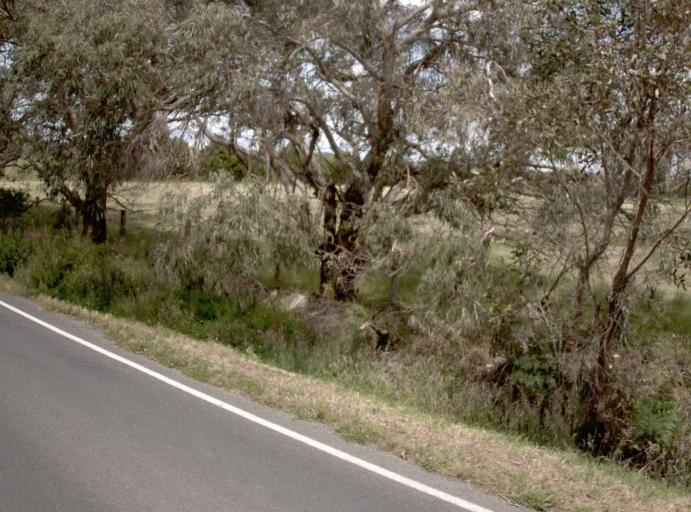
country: AU
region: Victoria
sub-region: Bass Coast
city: North Wonthaggi
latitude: -38.6136
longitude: 146.0165
